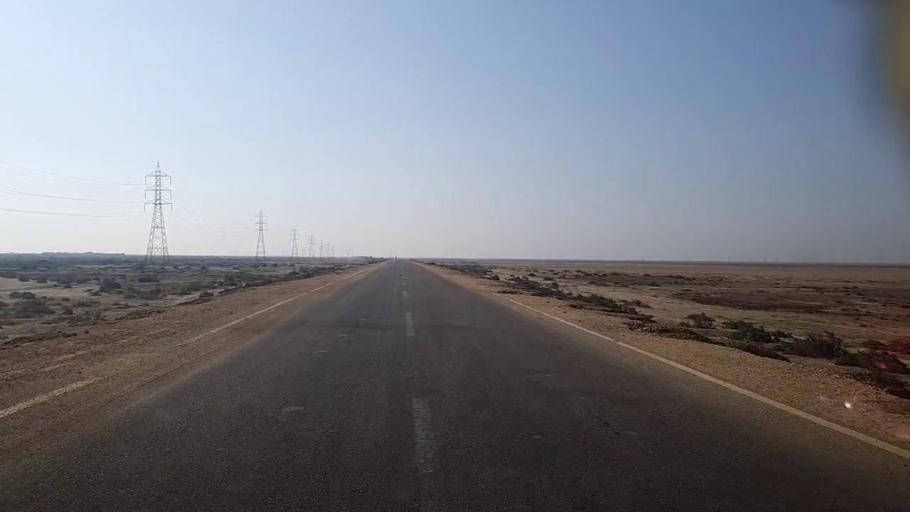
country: PK
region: Sindh
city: Mirpur Sakro
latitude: 24.6143
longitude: 67.4970
